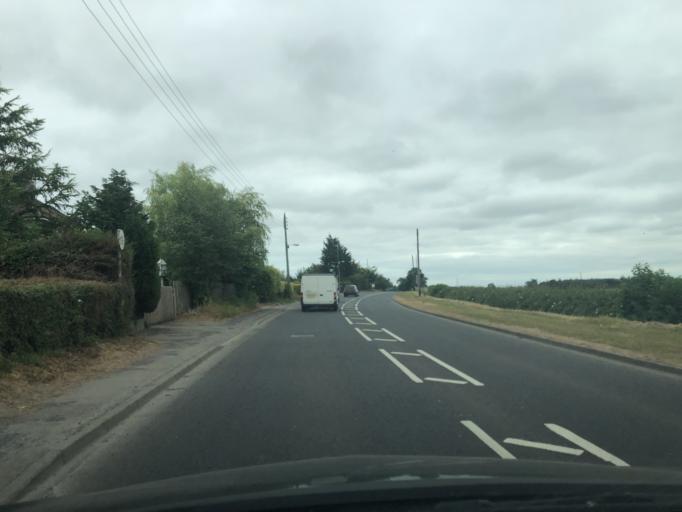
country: GB
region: England
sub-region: North Yorkshire
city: East Ayton
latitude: 54.2509
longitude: -0.4765
